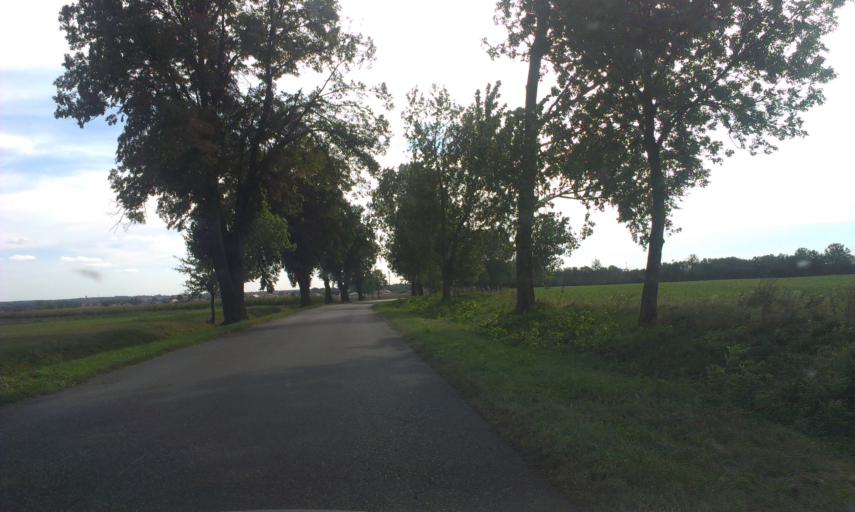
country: PL
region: Greater Poland Voivodeship
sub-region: Powiat zlotowski
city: Zlotow
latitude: 53.3830
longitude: 17.0169
